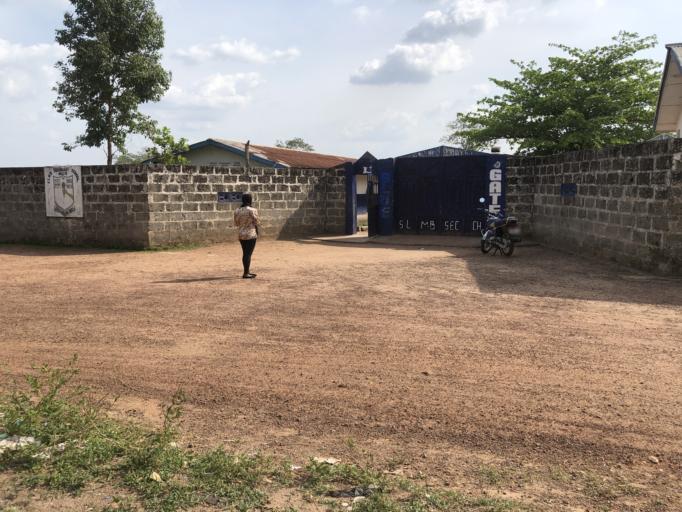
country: SL
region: Northern Province
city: Yonibana
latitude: 8.4618
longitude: -12.2196
